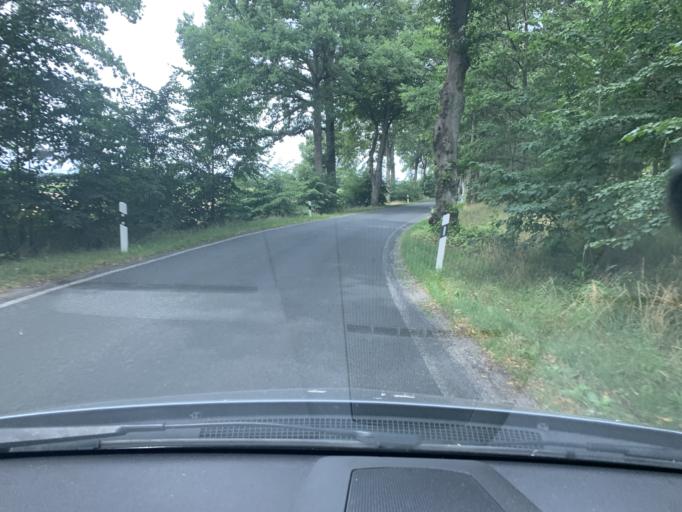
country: DE
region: Schleswig-Holstein
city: Gottin
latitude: 53.5352
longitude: 10.7005
